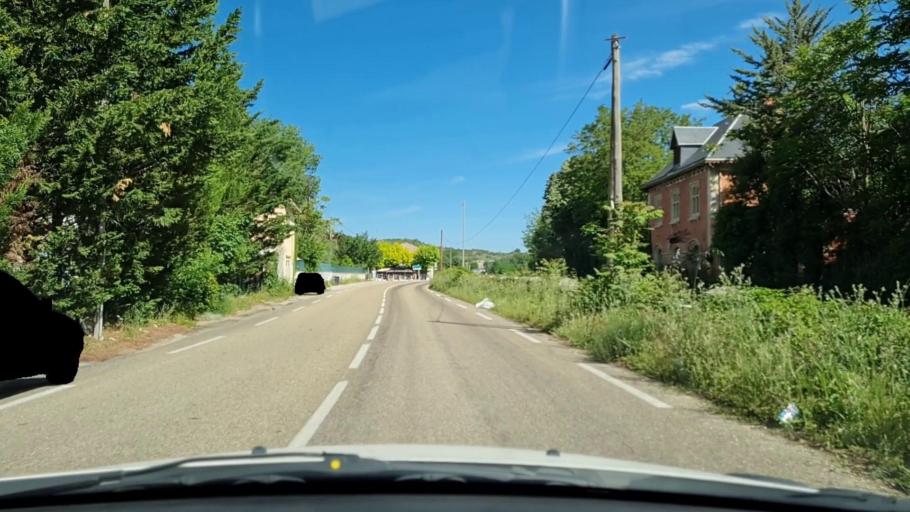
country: FR
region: Languedoc-Roussillon
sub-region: Departement du Gard
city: Vezenobres
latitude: 44.0156
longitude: 4.1582
